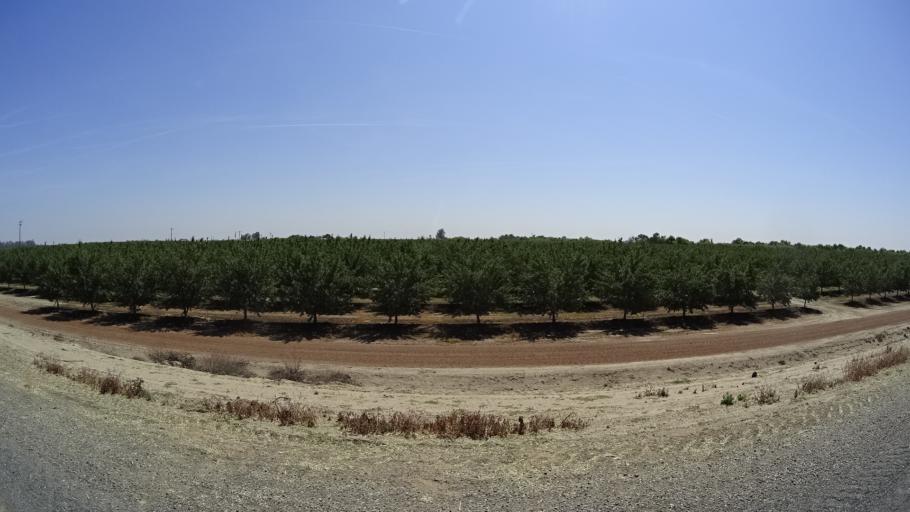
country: US
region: California
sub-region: Fresno County
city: Riverdale
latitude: 36.3901
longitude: -119.8514
